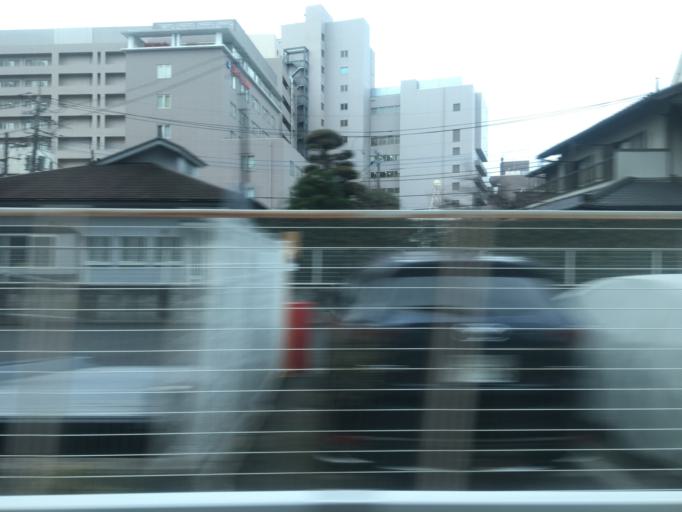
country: JP
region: Saitama
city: Ageoshimo
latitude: 35.9753
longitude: 139.5868
